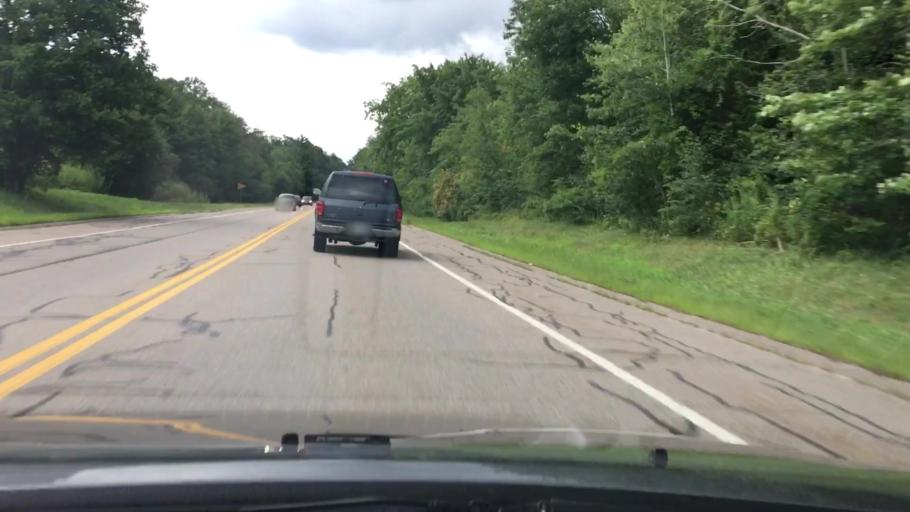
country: US
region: Massachusetts
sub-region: Norfolk County
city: Plainville
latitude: 41.9668
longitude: -71.3555
